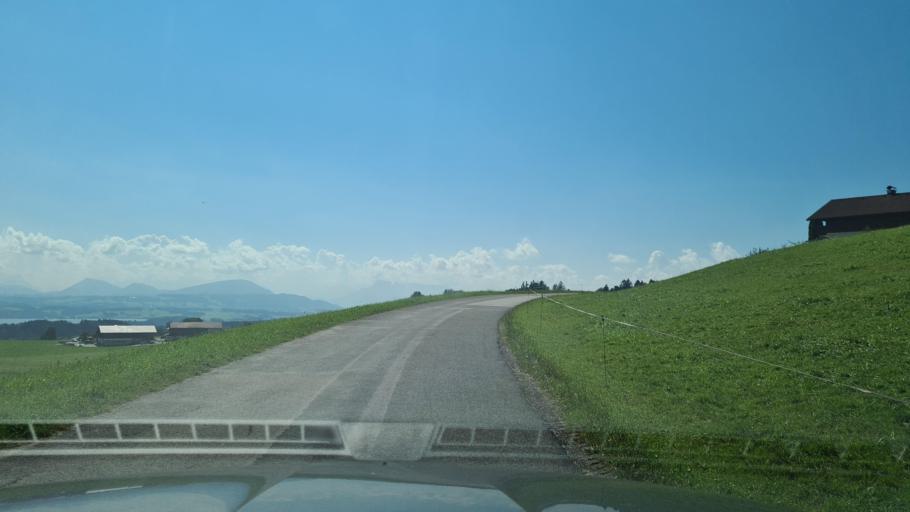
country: AT
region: Salzburg
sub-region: Politischer Bezirk Salzburg-Umgebung
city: Schleedorf
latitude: 47.9726
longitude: 13.1668
